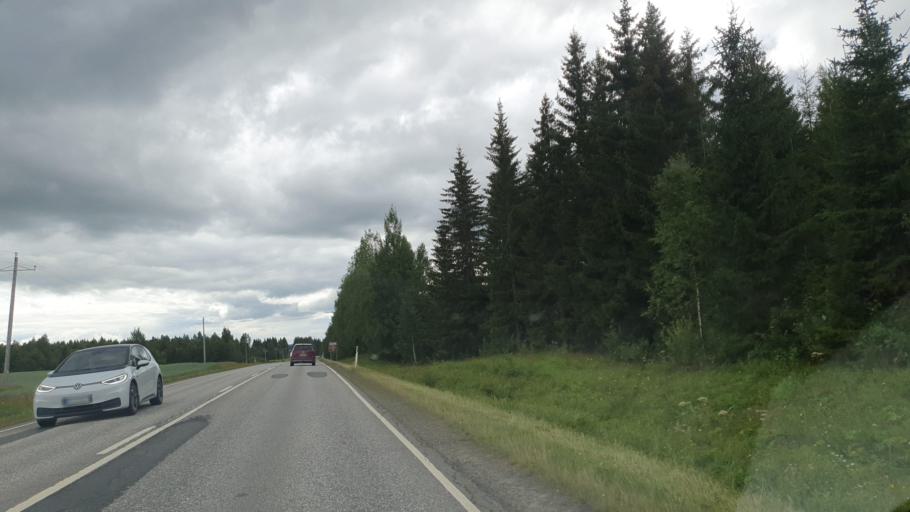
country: FI
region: Northern Savo
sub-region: Ylae-Savo
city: Sonkajaervi
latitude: 63.7317
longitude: 27.3761
